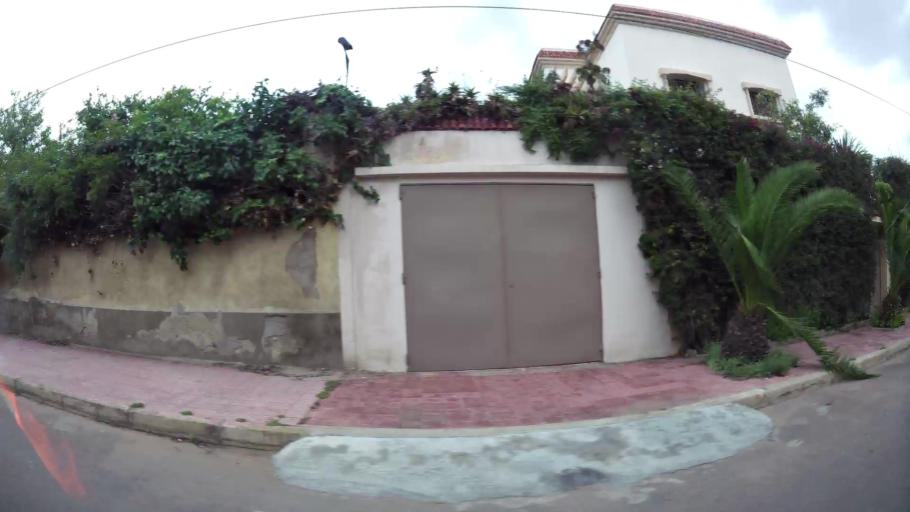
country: MA
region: Grand Casablanca
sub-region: Casablanca
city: Casablanca
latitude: 33.5566
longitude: -7.6155
